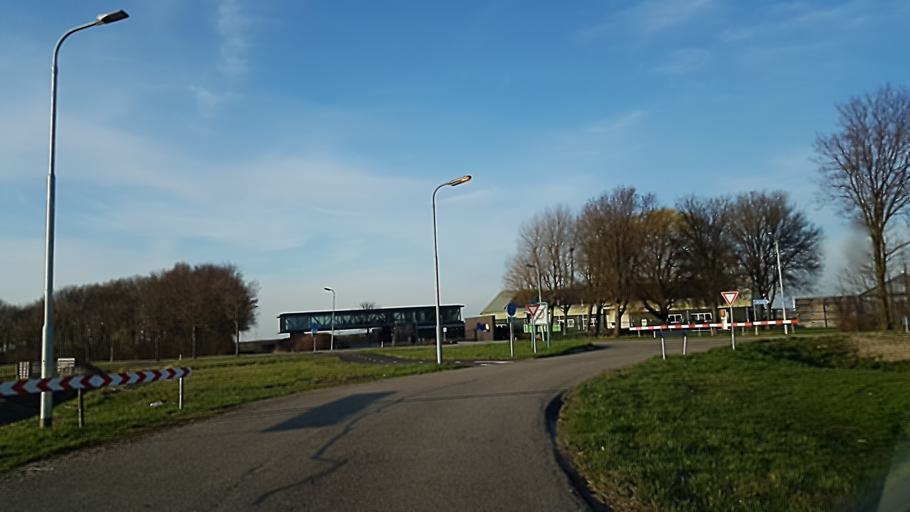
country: NL
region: North Brabant
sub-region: Gemeente Woensdrecht
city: Woensdrecht
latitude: 51.4062
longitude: 4.2104
